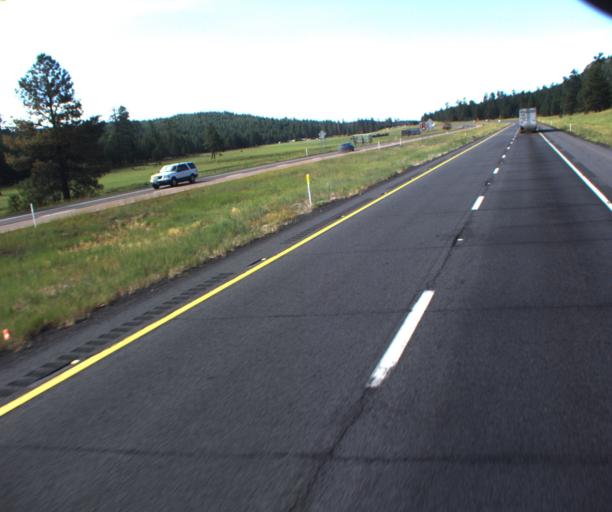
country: US
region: Arizona
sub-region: Coconino County
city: Mountainaire
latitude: 35.0280
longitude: -111.6851
